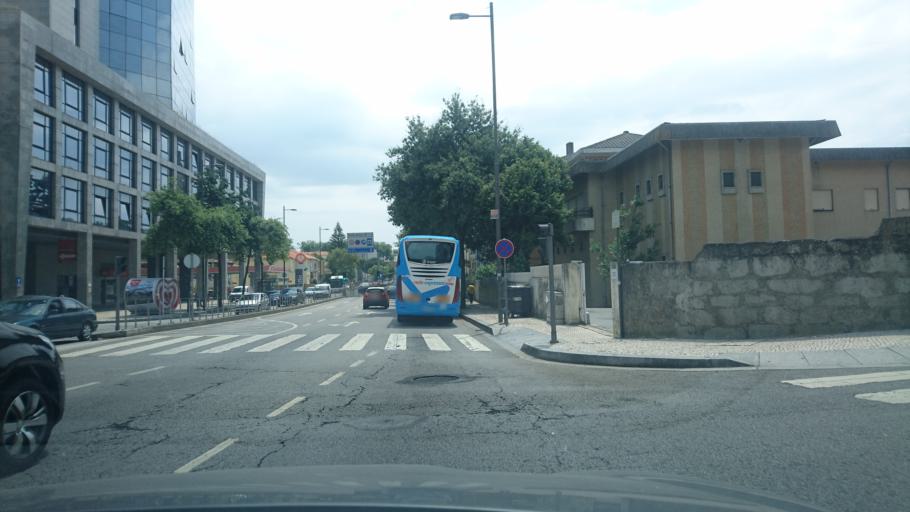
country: PT
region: Porto
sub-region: Porto
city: Porto
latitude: 41.1659
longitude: -8.5888
